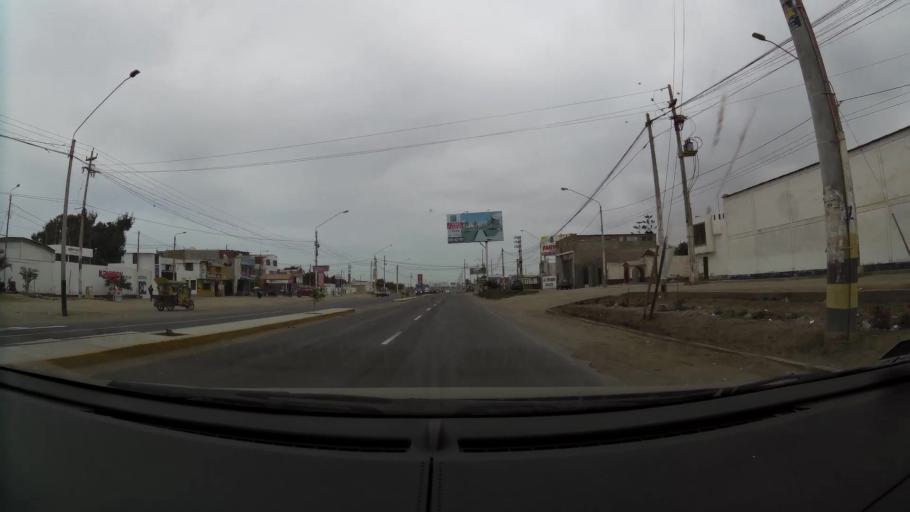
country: PE
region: La Libertad
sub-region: Provincia de Trujillo
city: Huanchaco
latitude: -8.0899
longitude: -79.0883
